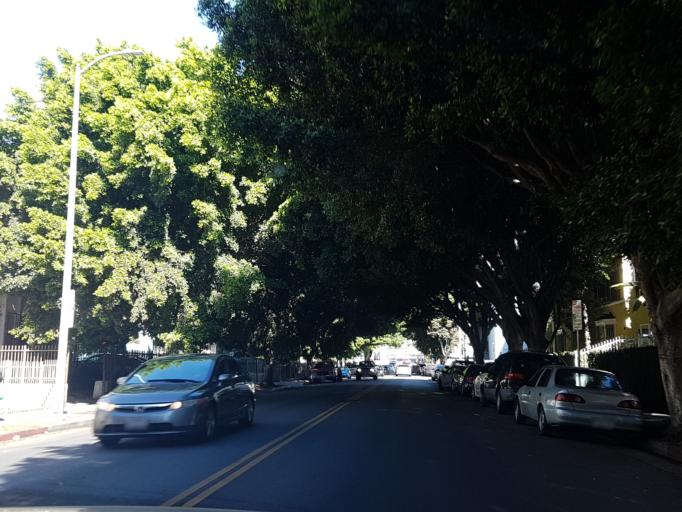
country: US
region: California
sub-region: Los Angeles County
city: Silver Lake
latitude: 34.0585
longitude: -118.3009
